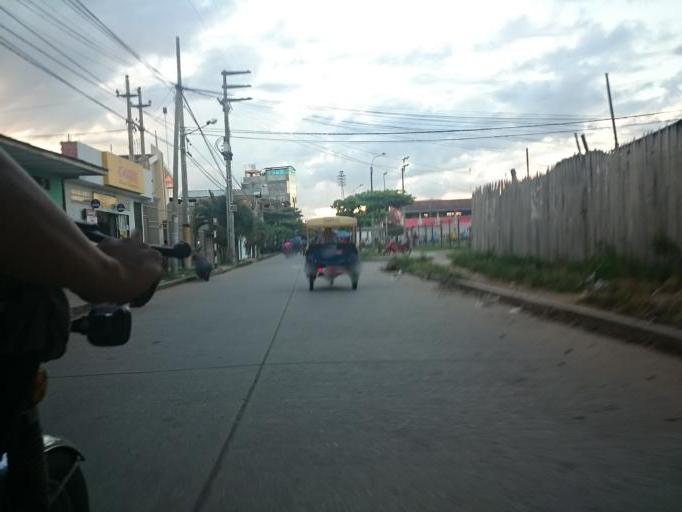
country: PE
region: Ucayali
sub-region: Provincia de Coronel Portillo
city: Pucallpa
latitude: -8.3806
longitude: -74.5384
